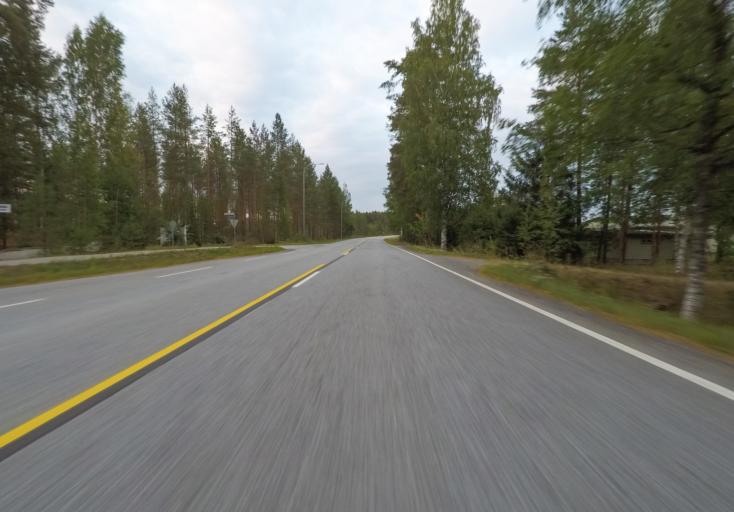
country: FI
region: Central Finland
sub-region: Jyvaeskylae
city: Toivakka
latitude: 62.1513
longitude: 26.1320
